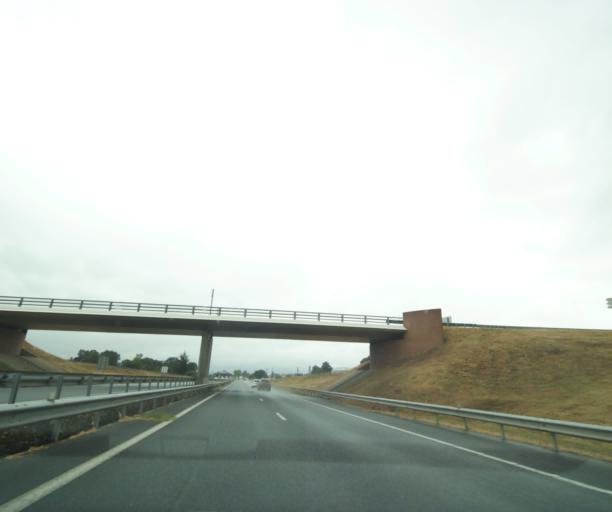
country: FR
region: Midi-Pyrenees
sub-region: Departement du Tarn
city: Castelnau-de-Levis
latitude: 43.9156
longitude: 2.0692
